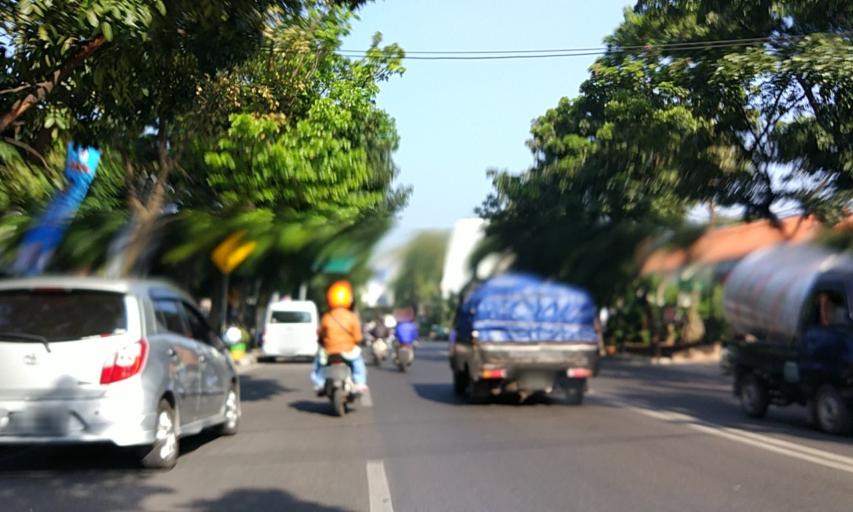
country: ID
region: West Java
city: Bandung
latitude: -6.8981
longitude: 107.6329
